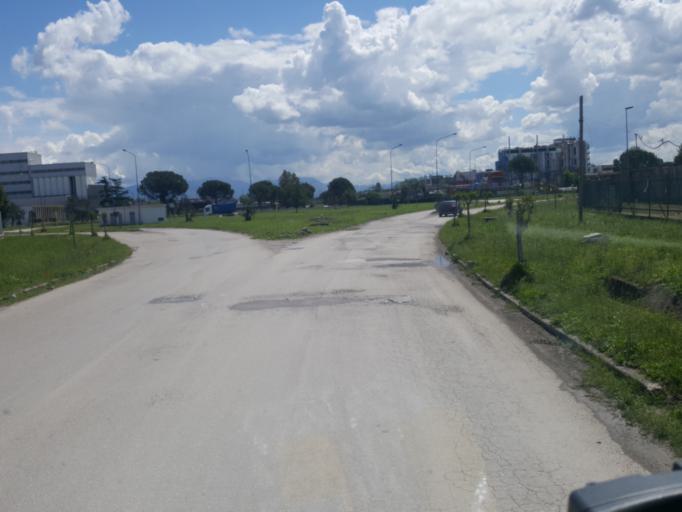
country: IT
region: Campania
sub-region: Provincia di Napoli
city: Pascarola
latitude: 40.9906
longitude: 14.3001
